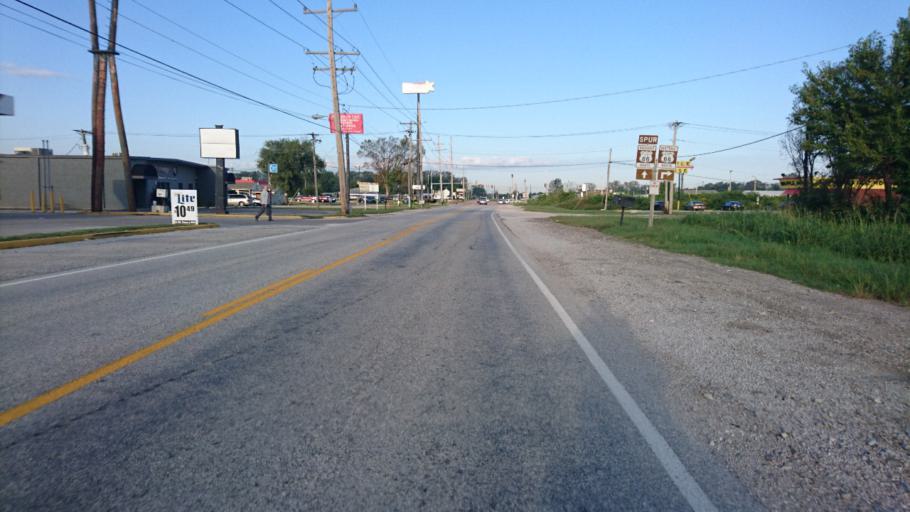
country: US
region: Illinois
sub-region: Madison County
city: Mitchell
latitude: 38.7621
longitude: -90.1221
